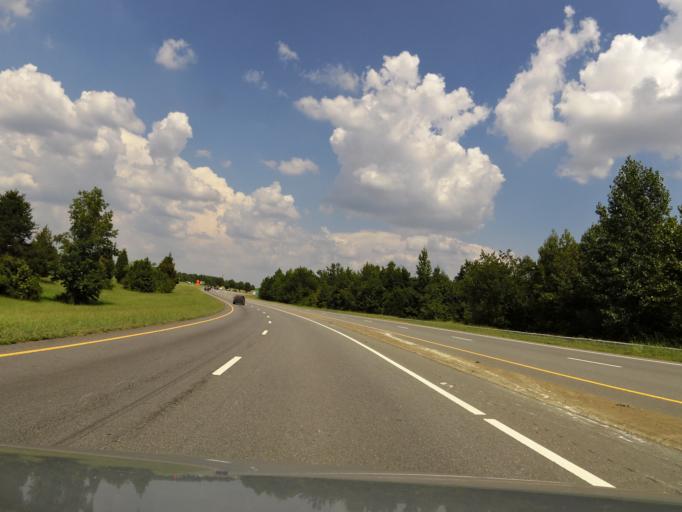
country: US
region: North Carolina
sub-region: Cleveland County
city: Kings Mountain
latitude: 35.2428
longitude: -81.3072
